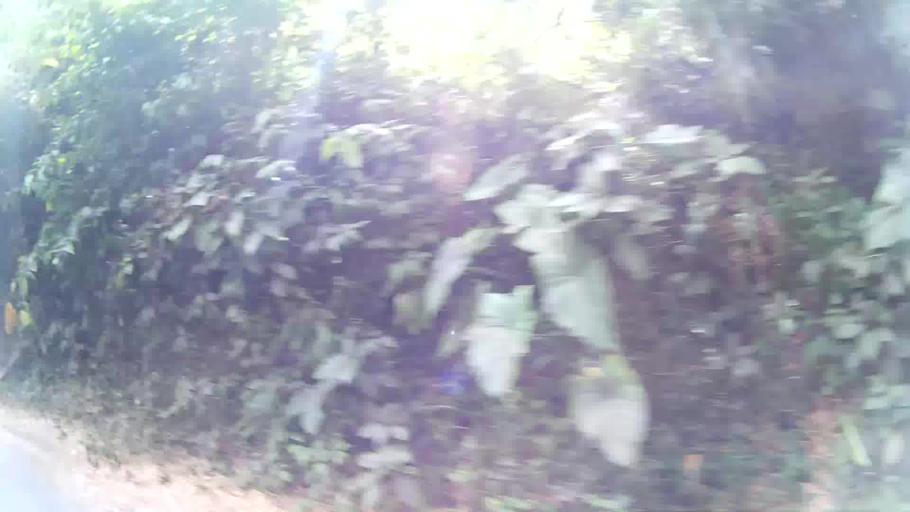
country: CO
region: Risaralda
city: Marsella
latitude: 4.8784
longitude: -75.7603
